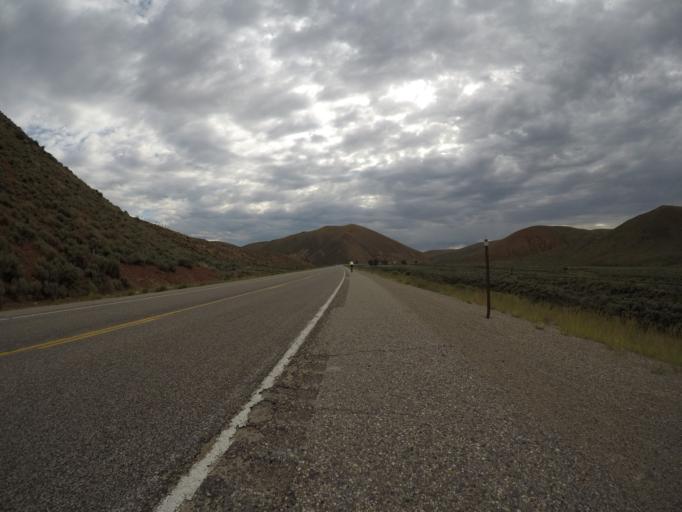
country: US
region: Wyoming
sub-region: Lincoln County
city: Kemmerer
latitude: 41.8228
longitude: -110.8333
